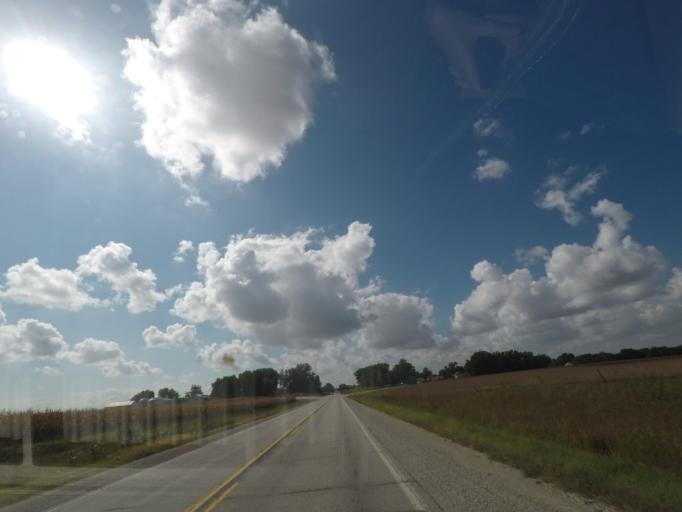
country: US
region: Iowa
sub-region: Story County
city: Nevada
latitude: 42.0262
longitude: -93.3095
